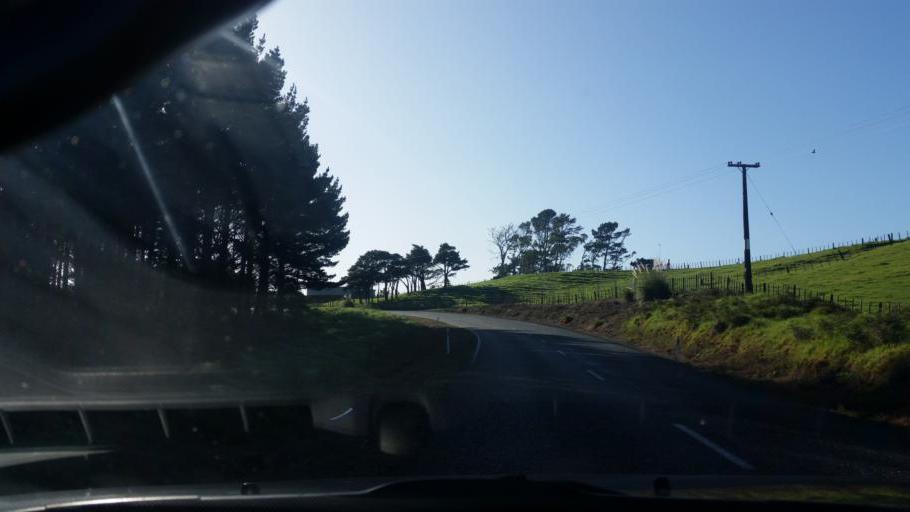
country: NZ
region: Auckland
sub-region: Auckland
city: Wellsford
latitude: -36.2273
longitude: 174.4505
